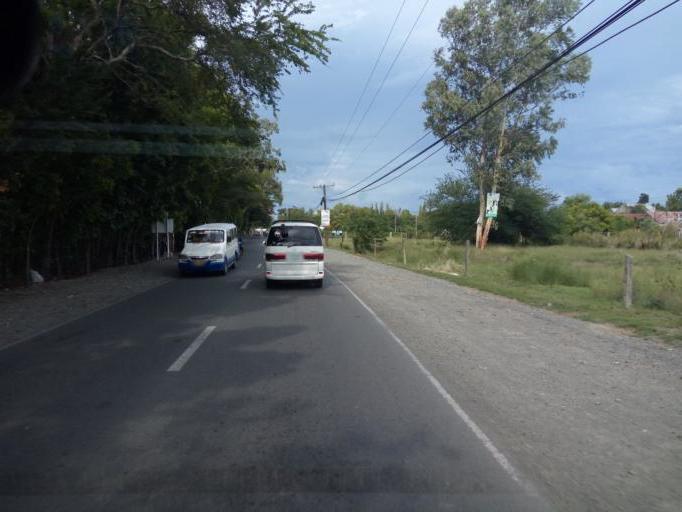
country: PH
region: Central Luzon
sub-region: Province of Nueva Ecija
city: Sibul
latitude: 15.7964
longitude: 120.9801
